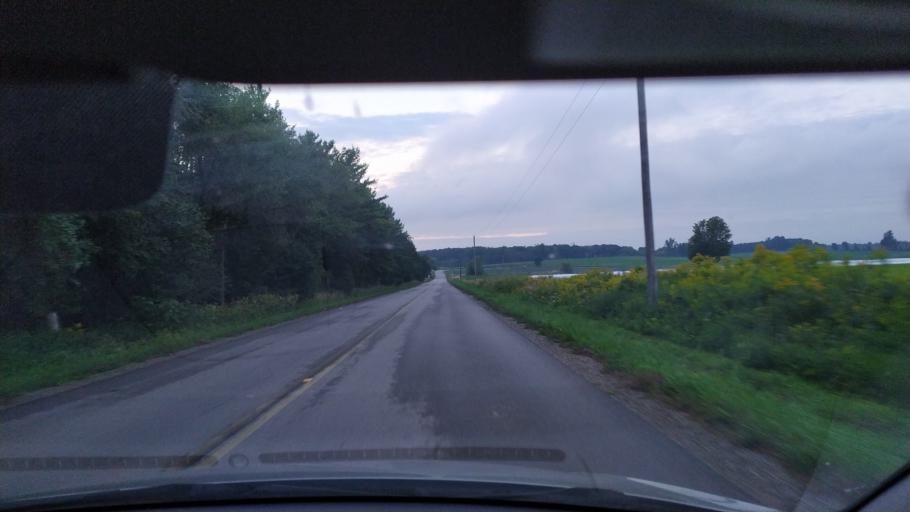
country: CA
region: Ontario
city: Kitchener
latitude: 43.3533
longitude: -80.6458
